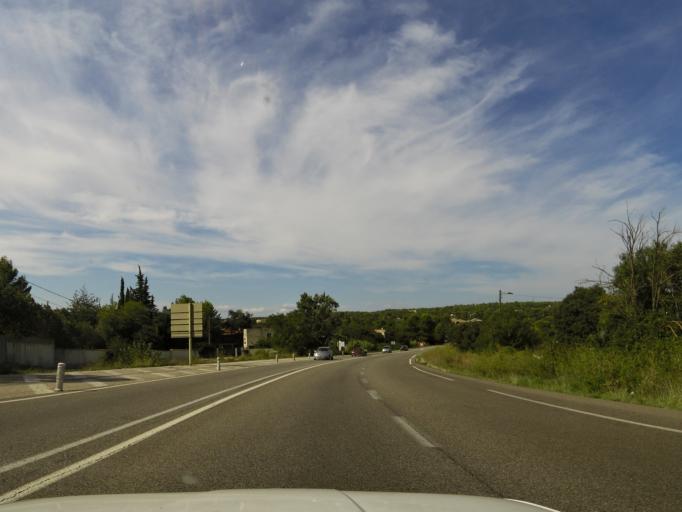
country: FR
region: Languedoc-Roussillon
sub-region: Departement du Gard
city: Nimes
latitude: 43.8436
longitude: 4.3169
